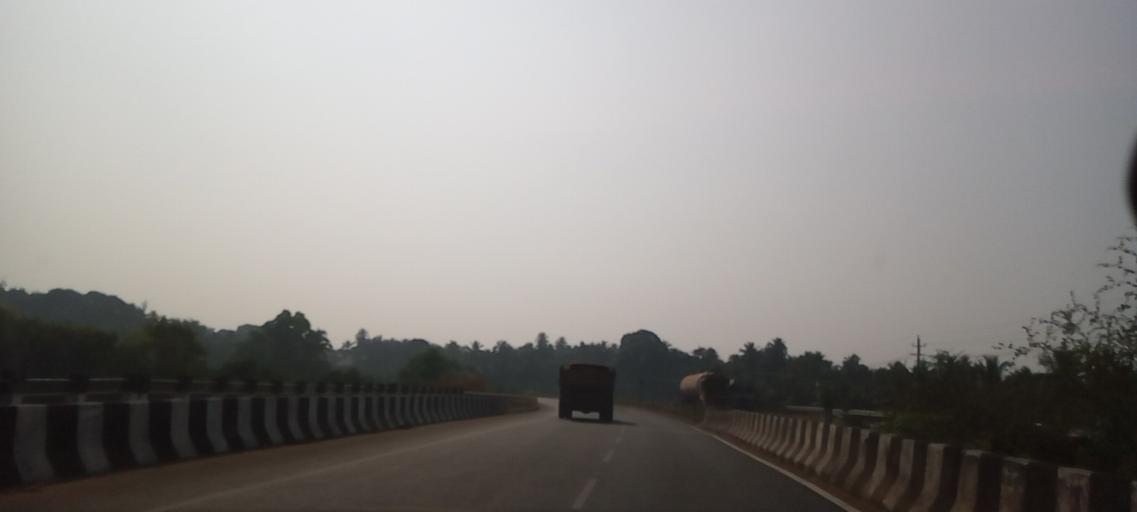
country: IN
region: Karnataka
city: Gangolli
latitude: 13.6793
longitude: 74.6872
